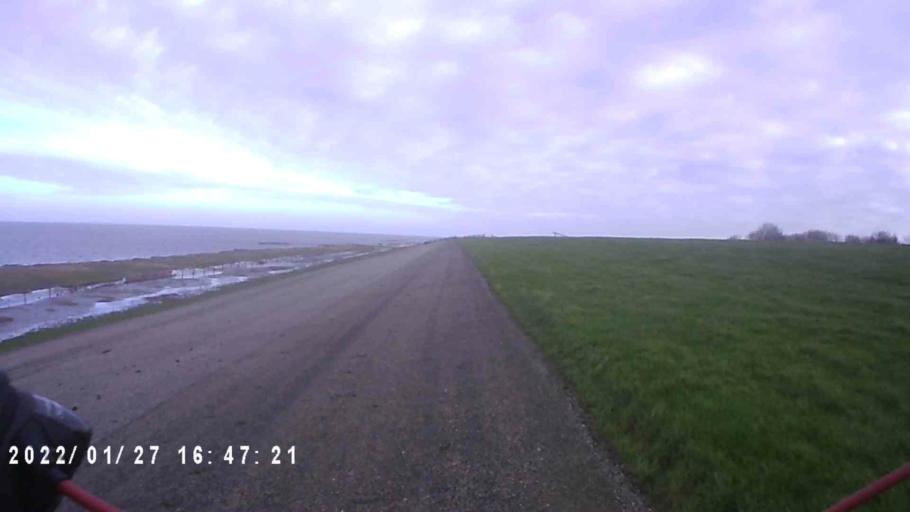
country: NL
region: Friesland
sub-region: Gemeente Dongeradeel
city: Ternaard
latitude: 53.4025
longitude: 6.0321
